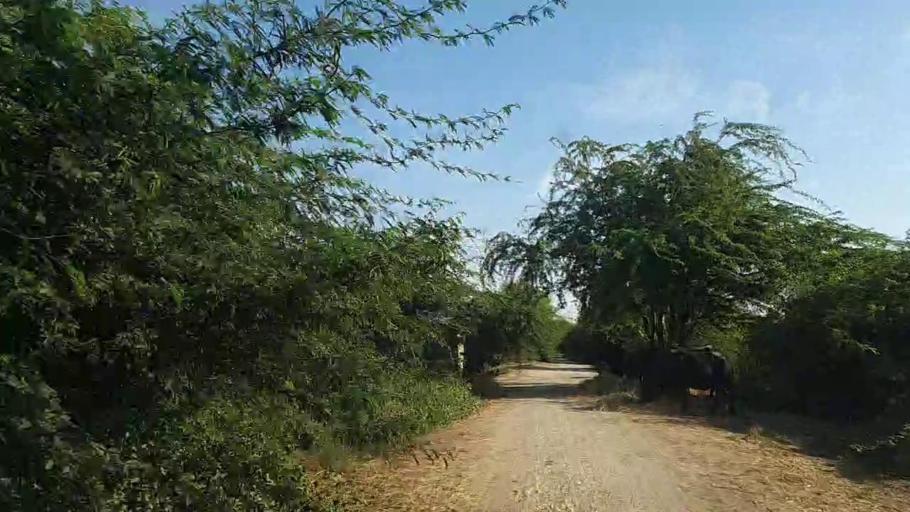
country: PK
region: Sindh
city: Bulri
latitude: 24.7852
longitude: 68.3503
